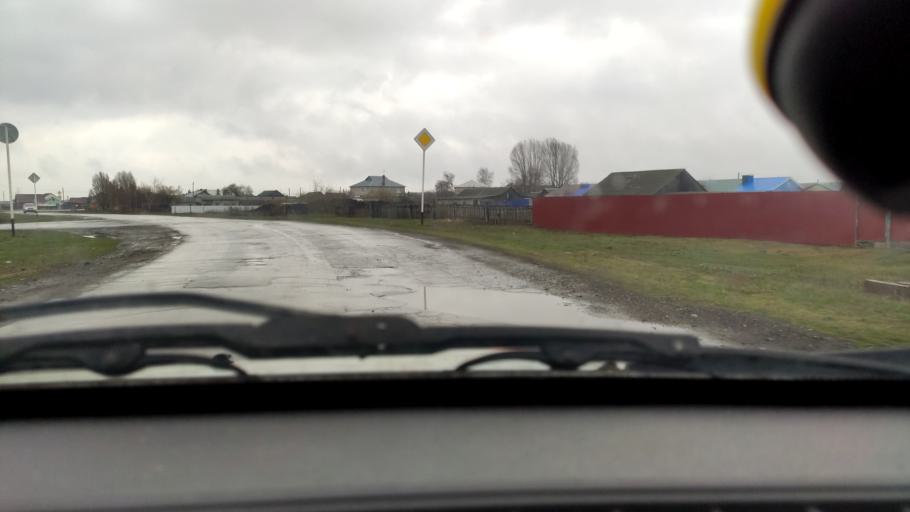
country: RU
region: Samara
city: Povolzhskiy
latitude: 53.6463
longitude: 49.6839
